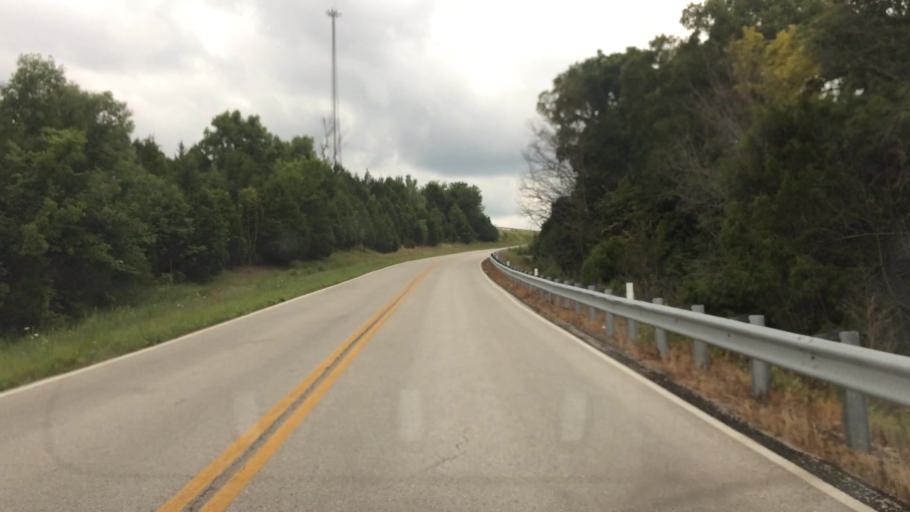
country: US
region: Missouri
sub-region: Webster County
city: Marshfield
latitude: 37.3028
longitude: -93.0079
